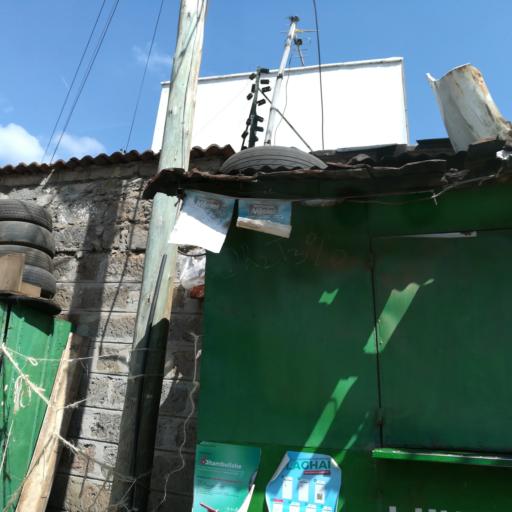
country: KE
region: Nairobi Area
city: Nairobi
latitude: -1.2958
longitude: 36.7999
